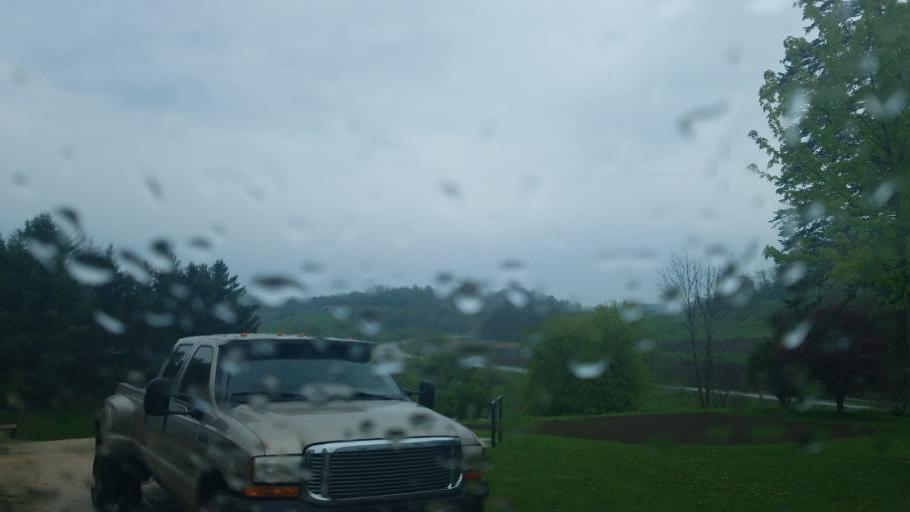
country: US
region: Wisconsin
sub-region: Vernon County
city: Hillsboro
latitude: 43.6470
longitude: -90.3503
